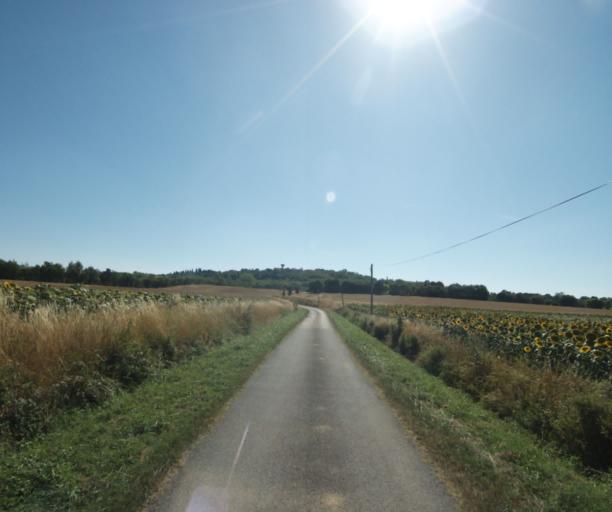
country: FR
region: Midi-Pyrenees
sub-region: Departement de la Haute-Garonne
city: Saint-Felix-Lauragais
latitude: 43.4968
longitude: 1.9071
